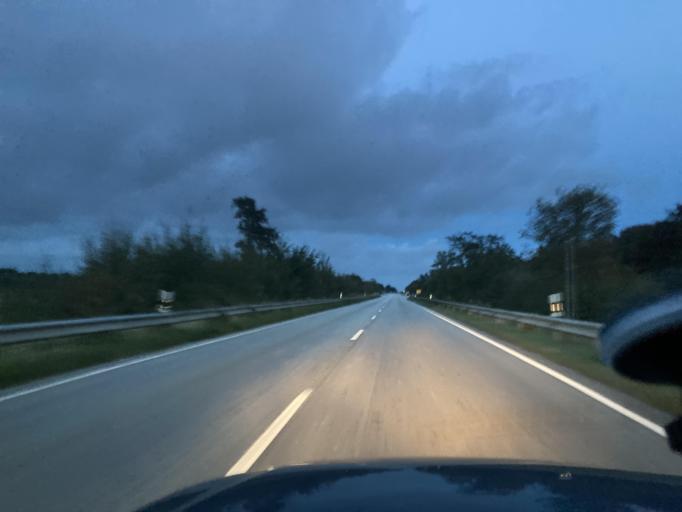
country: DE
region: Schleswig-Holstein
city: Tonning
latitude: 54.3247
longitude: 8.9417
